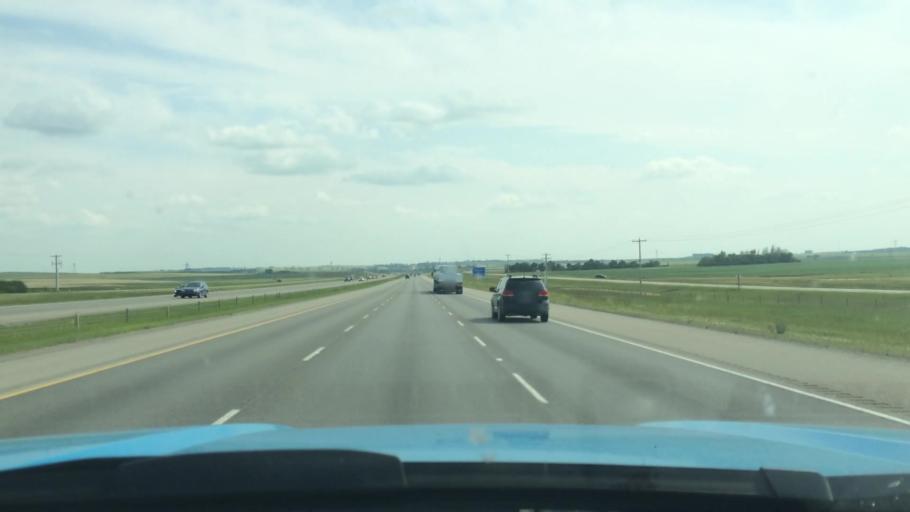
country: CA
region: Alberta
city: Crossfield
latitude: 51.4882
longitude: -114.0254
